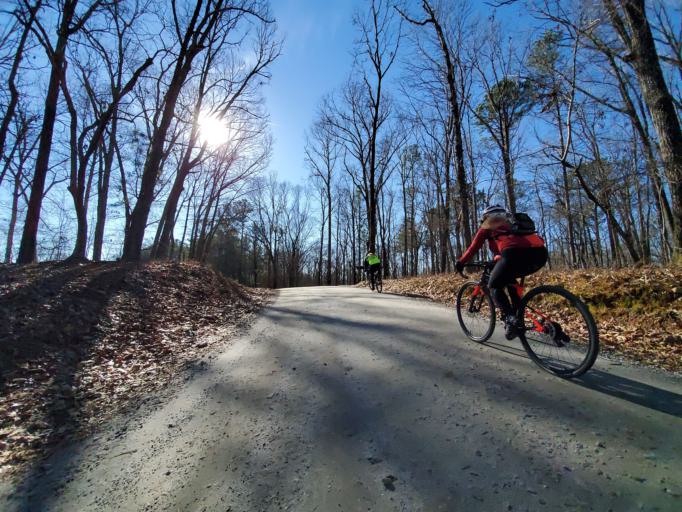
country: US
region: Georgia
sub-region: Fulton County
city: Chattahoochee Hills
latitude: 33.5593
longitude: -84.7808
